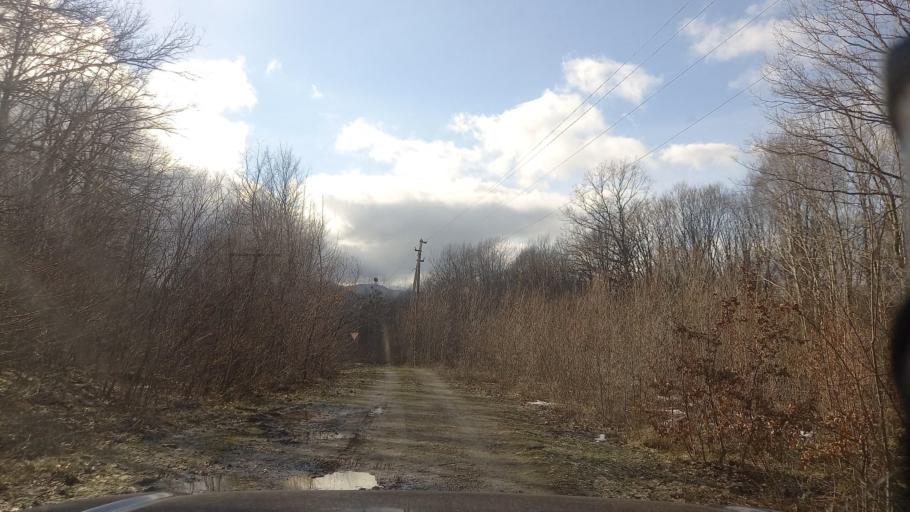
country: RU
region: Krasnodarskiy
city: Smolenskaya
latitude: 44.5852
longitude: 38.8124
